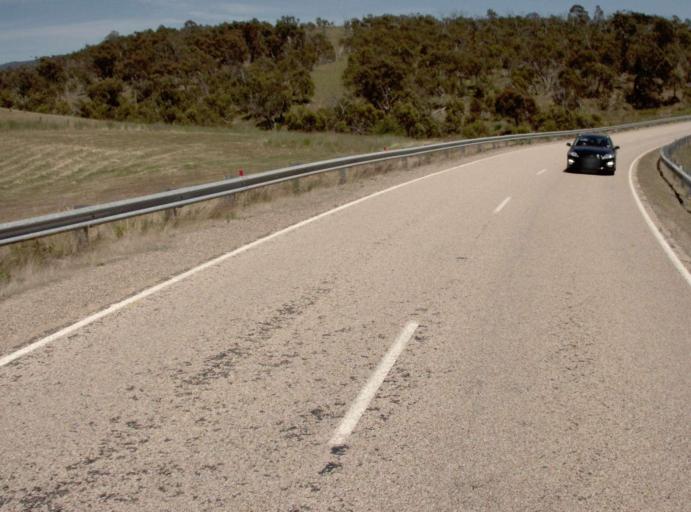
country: AU
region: Victoria
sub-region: Alpine
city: Mount Beauty
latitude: -37.1219
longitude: 147.6256
